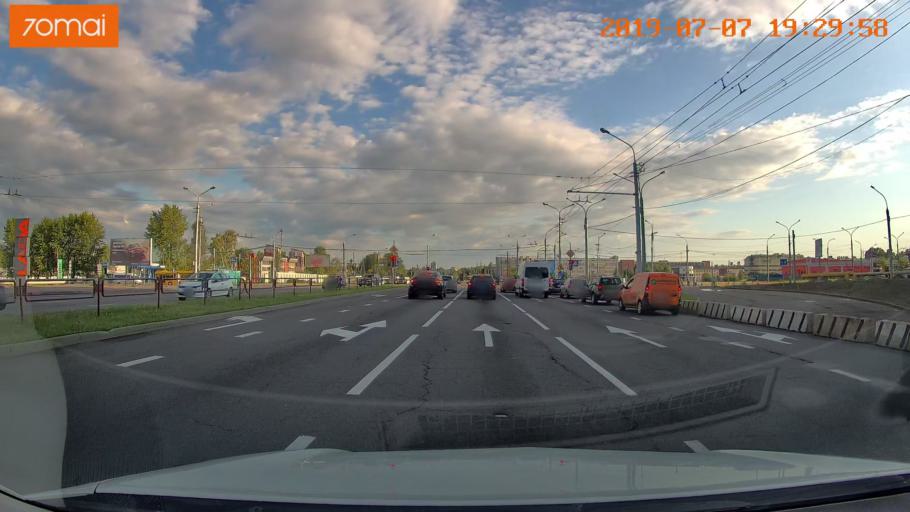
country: BY
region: Minsk
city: Syenitsa
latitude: 53.8443
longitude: 27.5344
